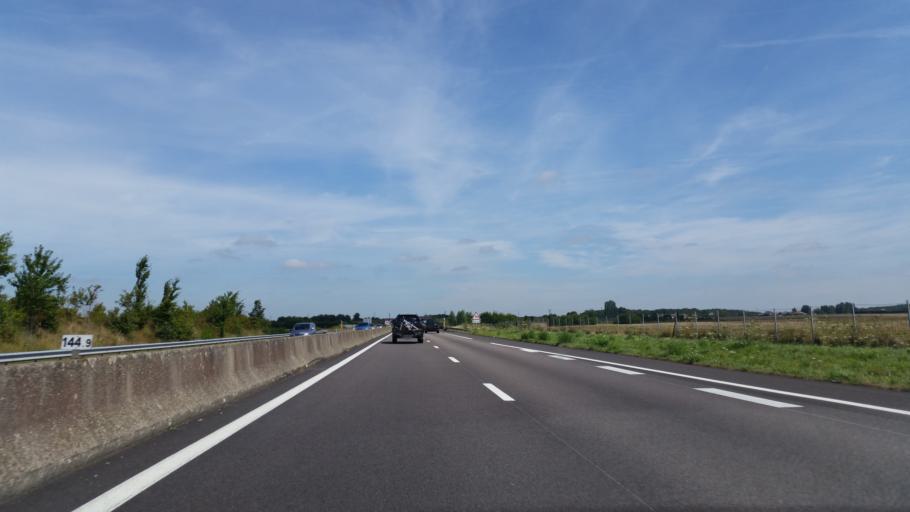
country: FR
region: Haute-Normandie
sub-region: Departement de la Seine-Maritime
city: Aumale
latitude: 49.7657
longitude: 1.7090
